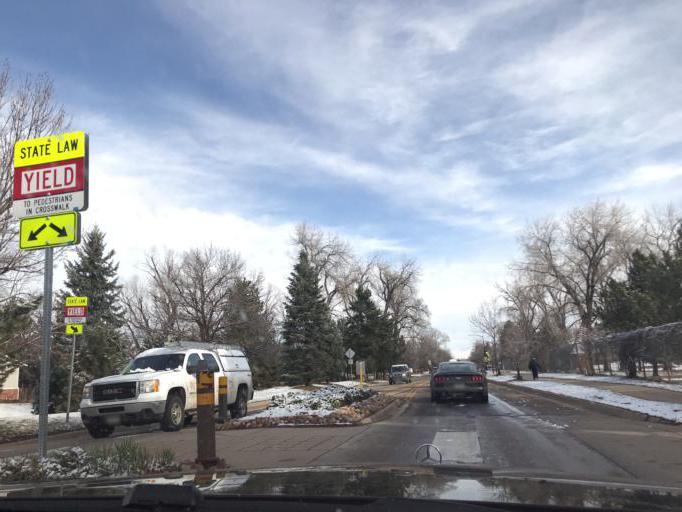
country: US
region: Colorado
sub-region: Boulder County
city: Boulder
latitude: 40.0095
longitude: -105.2253
